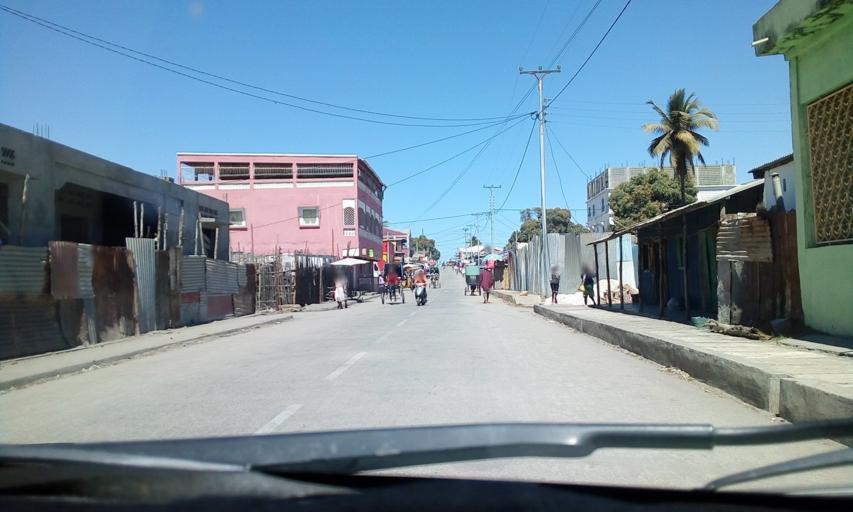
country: MG
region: Boeny
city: Mahajanga
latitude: -15.7153
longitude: 46.3223
